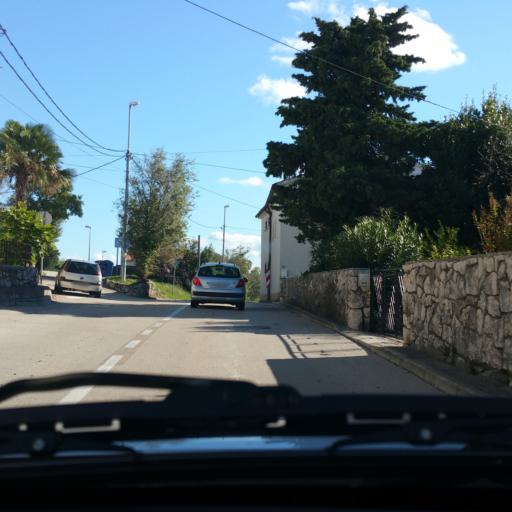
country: HR
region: Primorsko-Goranska
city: Omisalj
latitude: 45.2094
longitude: 14.5579
